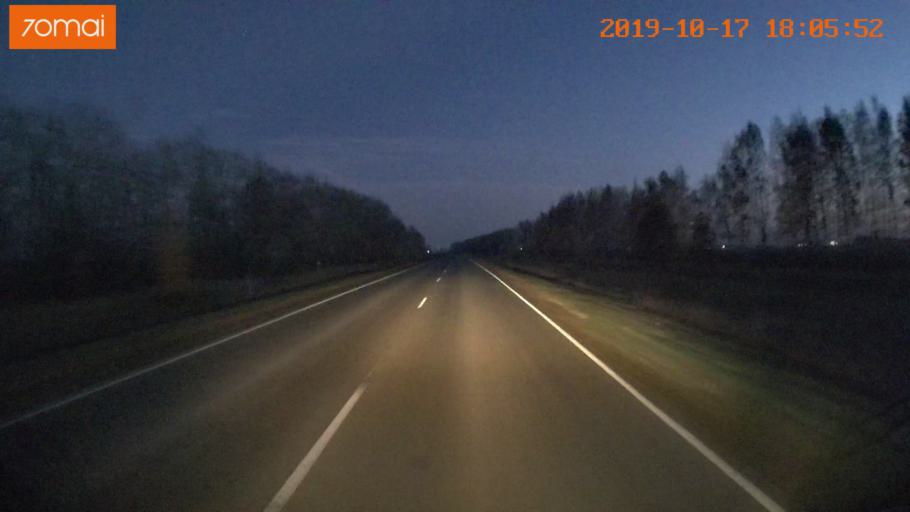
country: RU
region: Tula
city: Kurkino
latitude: 53.4600
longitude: 38.6489
